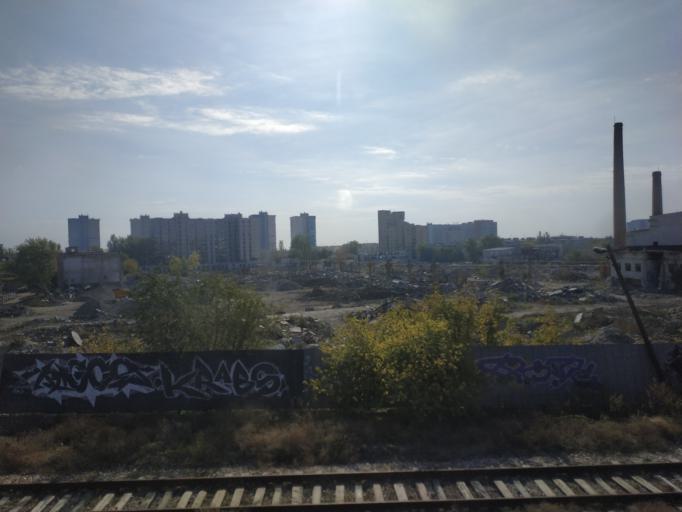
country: RU
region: Volgograd
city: Volgograd
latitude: 48.7332
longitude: 44.5360
